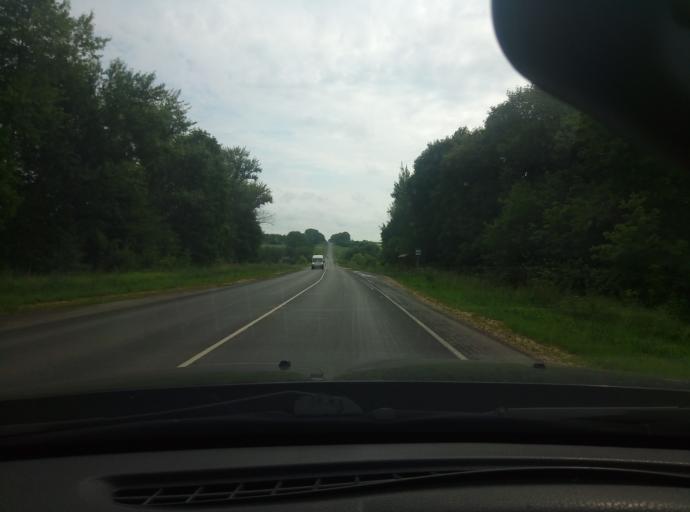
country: RU
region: Tula
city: Severo-Zadonsk
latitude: 53.9684
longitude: 38.4312
